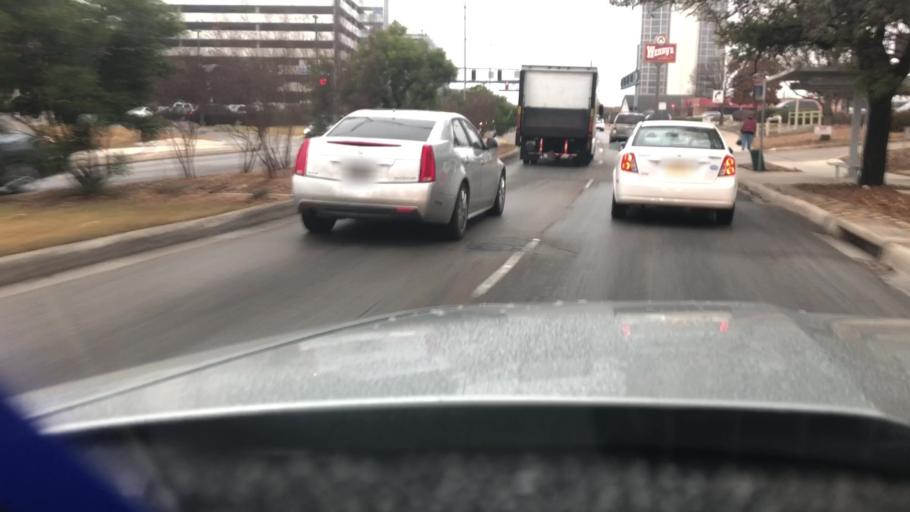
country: US
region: Texas
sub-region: Bexar County
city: Balcones Heights
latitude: 29.5114
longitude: -98.5799
